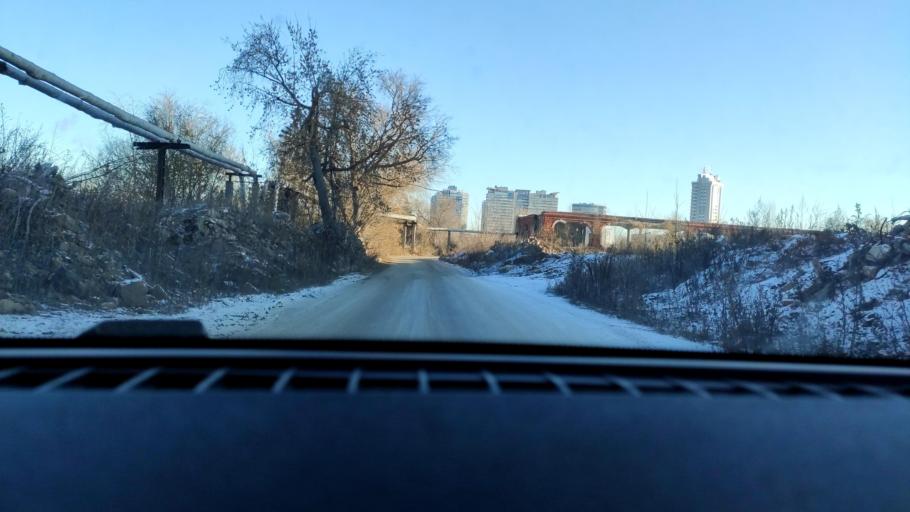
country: RU
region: Samara
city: Samara
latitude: 53.2179
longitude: 50.1428
